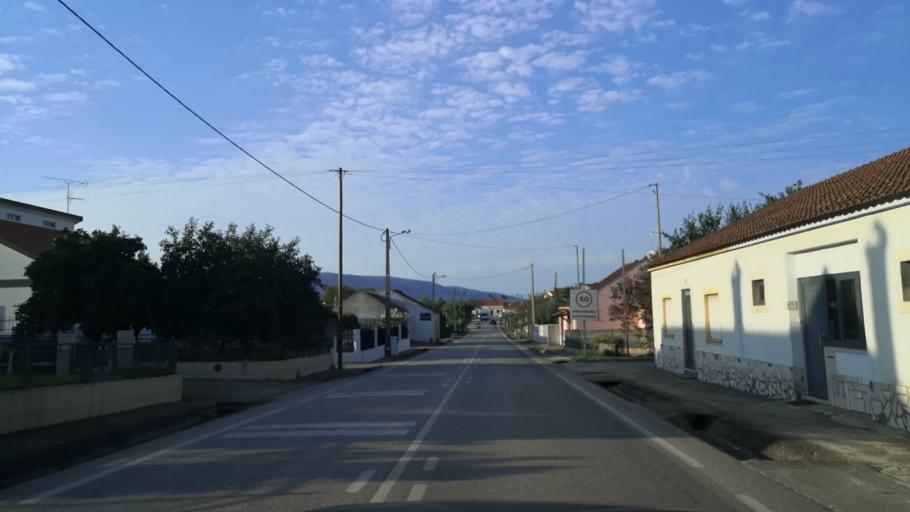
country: PT
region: Santarem
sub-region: Alcanena
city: Alcanena
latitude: 39.4489
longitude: -8.6227
